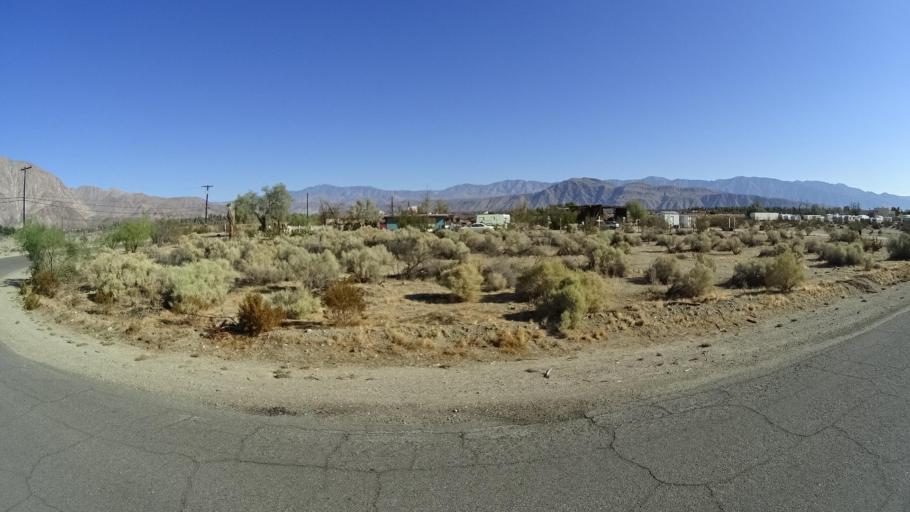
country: US
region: California
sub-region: San Diego County
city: Borrego Springs
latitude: 33.2624
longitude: -116.3732
